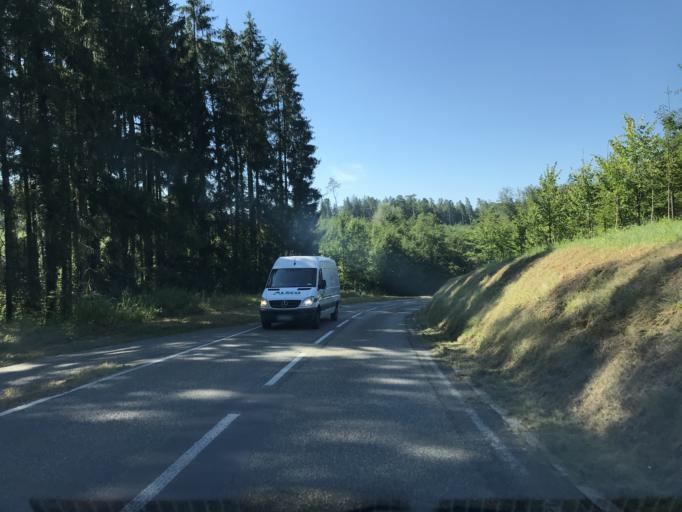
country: DE
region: Baden-Wuerttemberg
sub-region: Freiburg Region
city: Schopfheim
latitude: 47.6127
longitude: 7.8130
